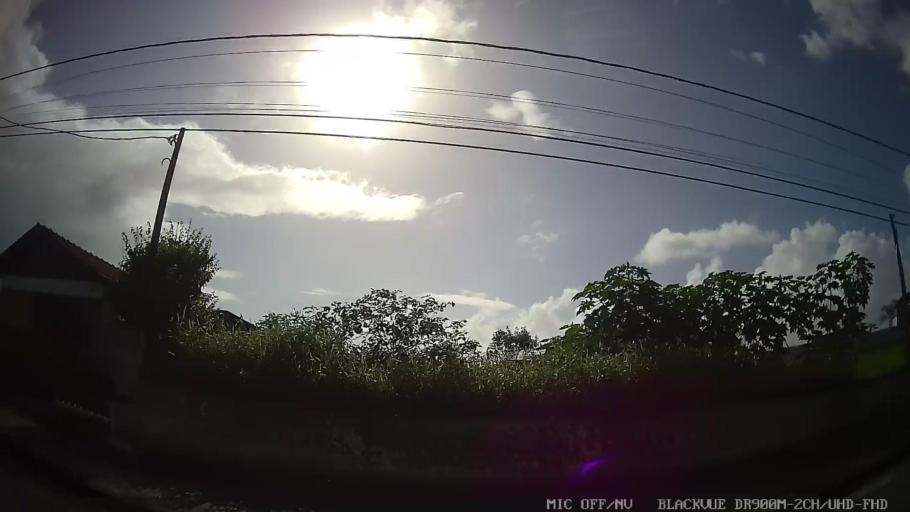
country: BR
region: Sao Paulo
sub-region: Itanhaem
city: Itanhaem
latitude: -24.2080
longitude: -46.8360
